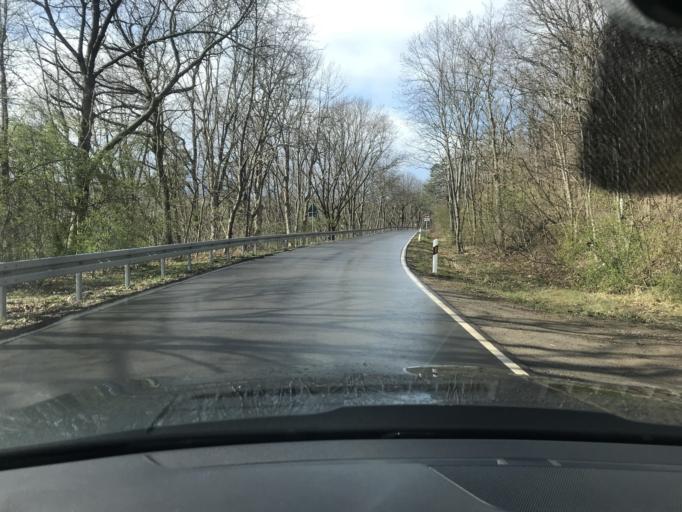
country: DE
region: Saxony-Anhalt
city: Hoym
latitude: 51.7070
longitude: 11.3161
